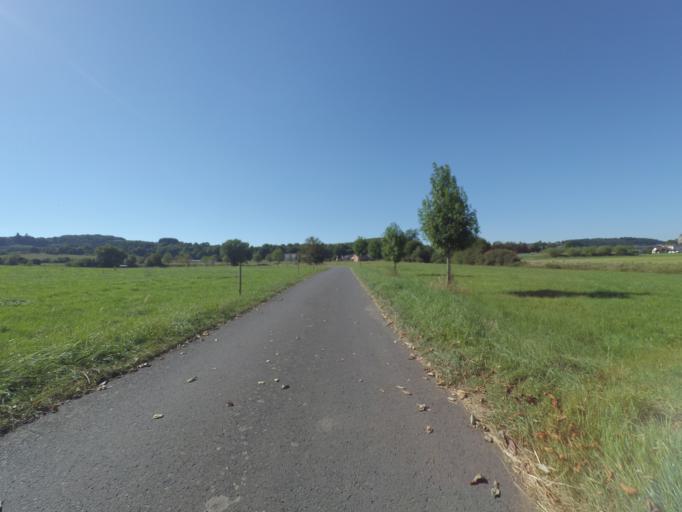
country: DE
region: Rheinland-Pfalz
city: Gillenfeld
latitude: 50.1199
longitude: 6.9054
